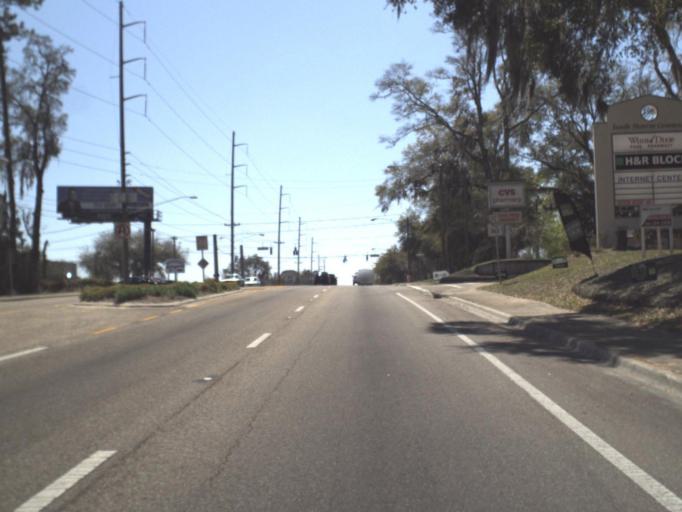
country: US
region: Florida
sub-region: Leon County
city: Tallahassee
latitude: 30.4069
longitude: -84.2807
